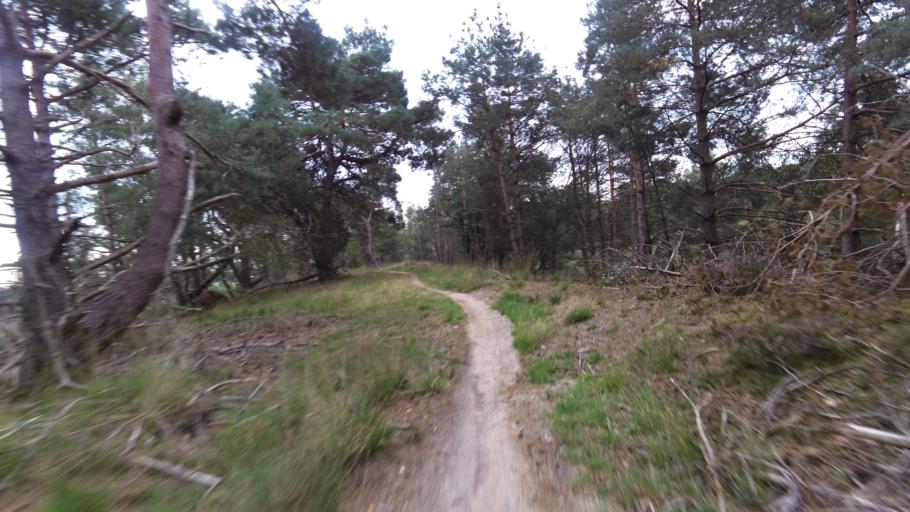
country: NL
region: Gelderland
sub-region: Gemeente Apeldoorn
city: Apeldoorn
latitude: 52.1976
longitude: 5.8679
